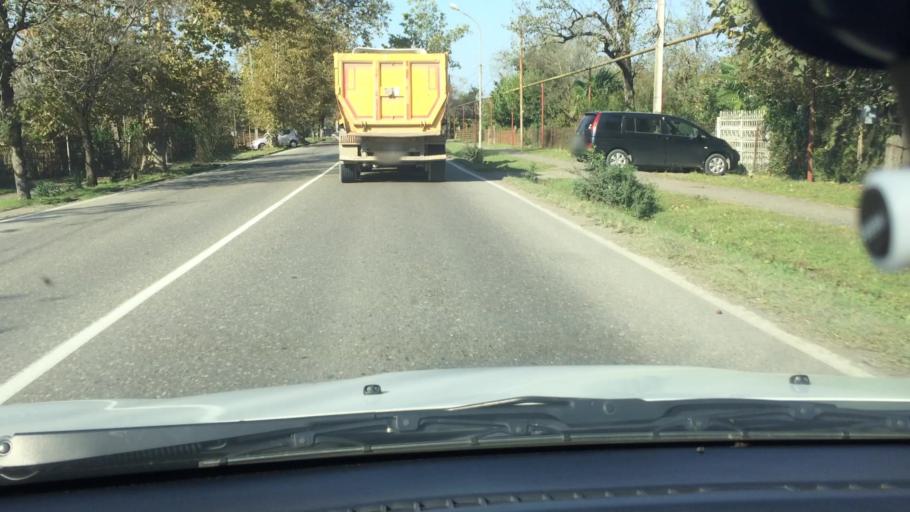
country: GE
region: Guria
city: Lanchkhuti
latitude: 42.0894
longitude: 42.0266
